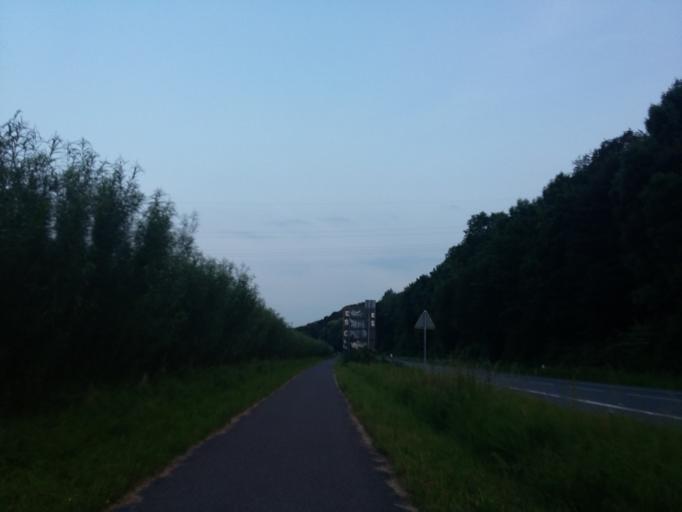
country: DE
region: North Rhine-Westphalia
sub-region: Regierungsbezirk Detmold
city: Vlotho
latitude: 52.1933
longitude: 8.8529
